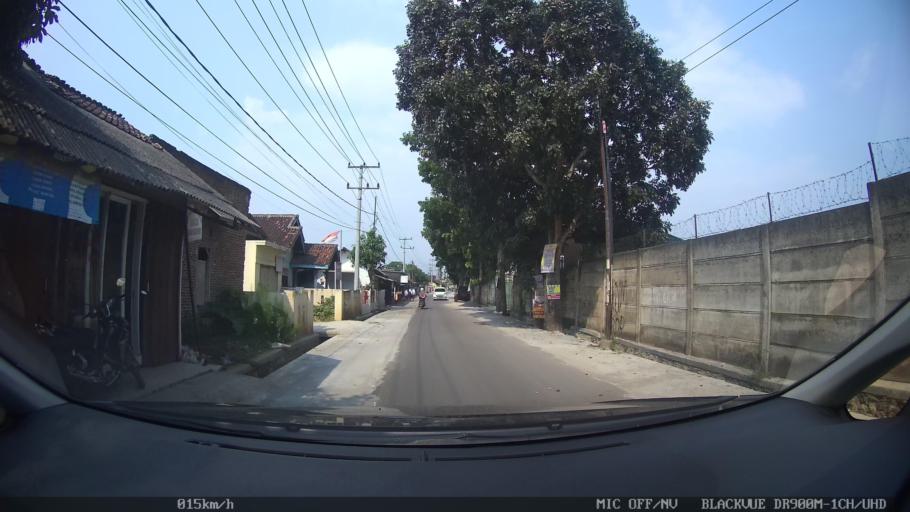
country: ID
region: Lampung
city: Natar
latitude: -5.3489
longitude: 105.2182
